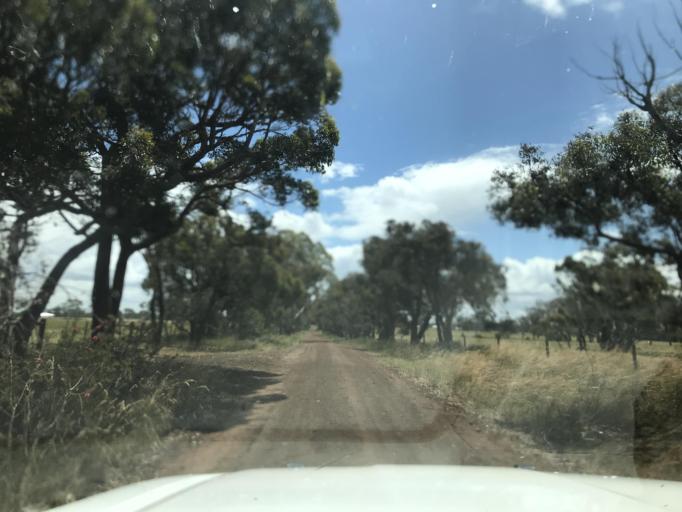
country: AU
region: South Australia
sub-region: Wattle Range
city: Penola
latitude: -37.1247
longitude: 141.2934
